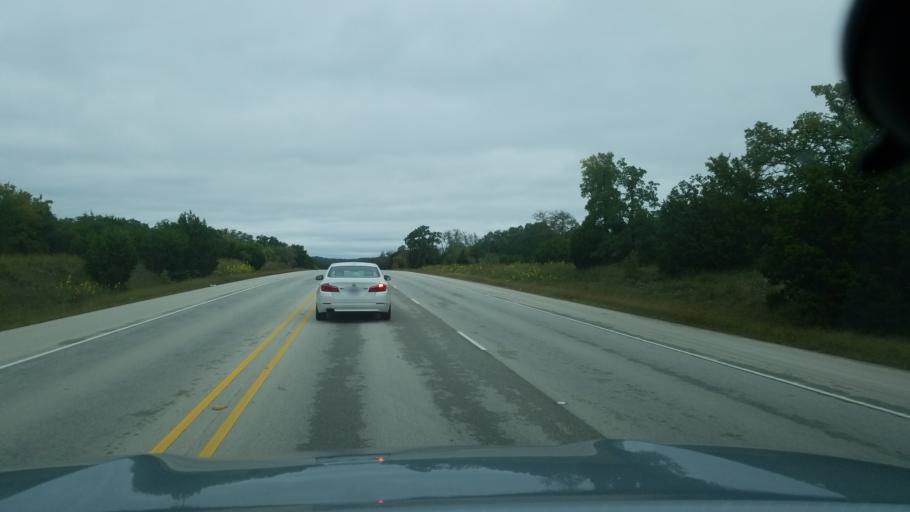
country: US
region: Texas
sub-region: Blanco County
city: Blanco
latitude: 30.0076
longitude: -98.4056
